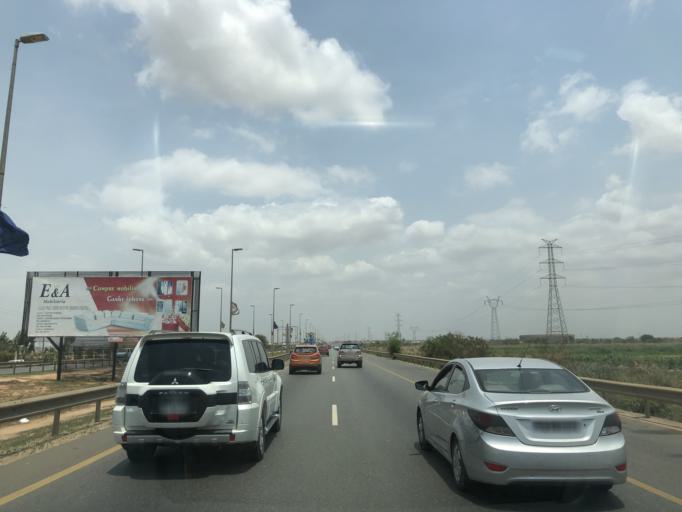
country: AO
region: Luanda
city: Luanda
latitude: -8.9736
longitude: 13.2700
